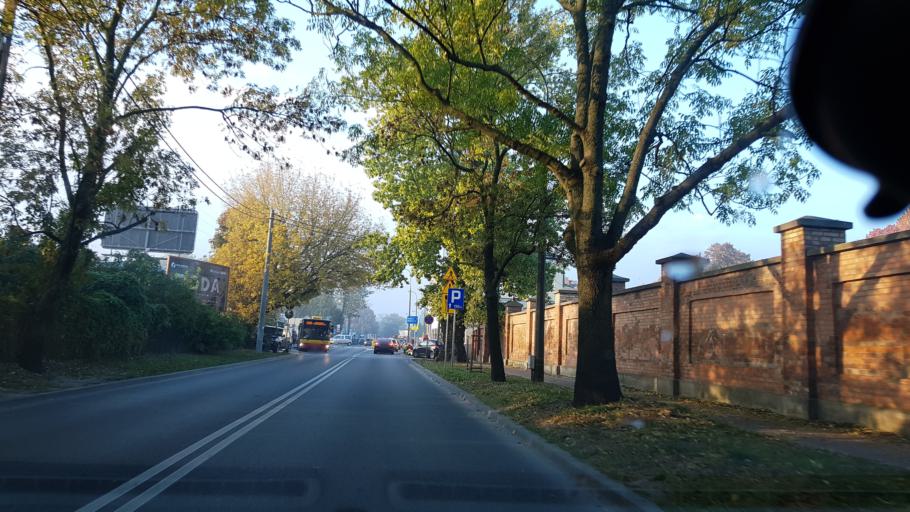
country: PL
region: Masovian Voivodeship
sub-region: Warszawa
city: Targowek
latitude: 52.2795
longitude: 21.0453
